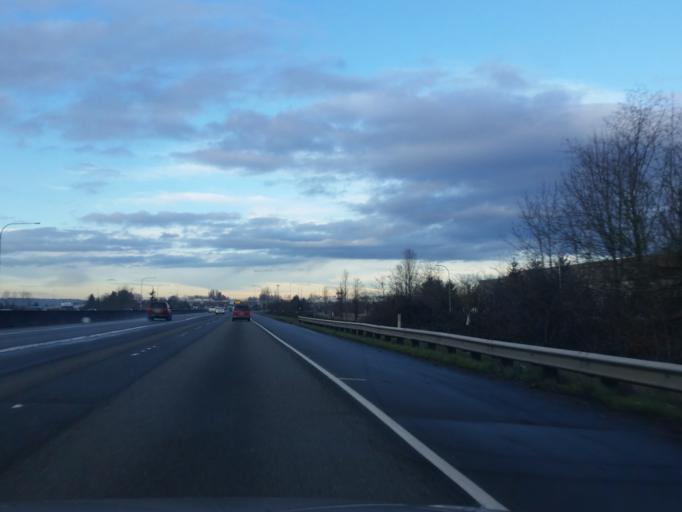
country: US
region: Washington
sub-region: King County
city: Kent
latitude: 47.3475
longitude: -122.2446
